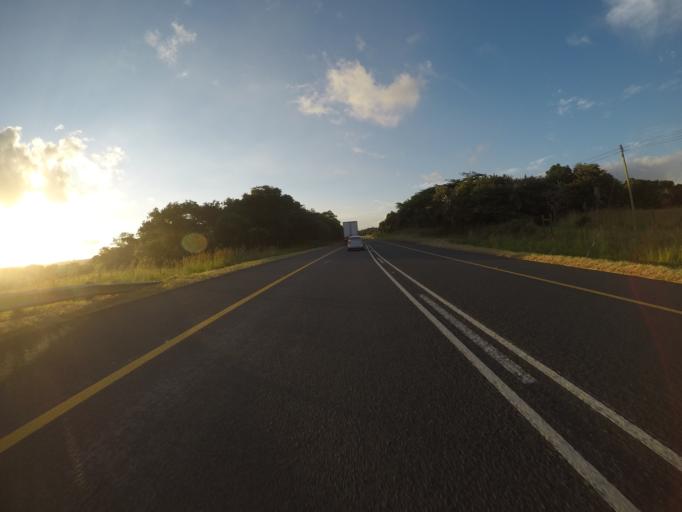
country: ZA
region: KwaZulu-Natal
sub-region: uThungulu District Municipality
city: Richards Bay
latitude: -28.6946
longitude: 32.0088
